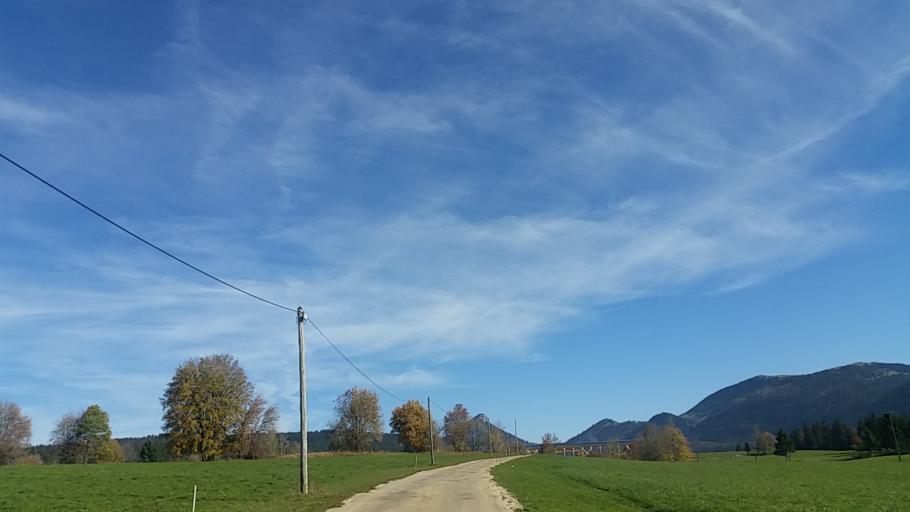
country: FR
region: Franche-Comte
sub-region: Departement du Doubs
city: Jougne
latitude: 46.7682
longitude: 6.4023
